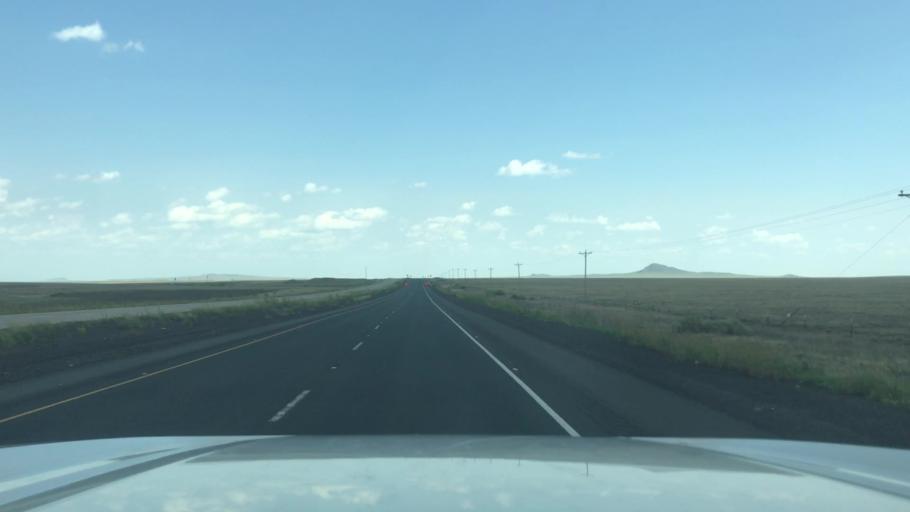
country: US
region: New Mexico
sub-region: Union County
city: Clayton
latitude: 36.6275
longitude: -103.7074
